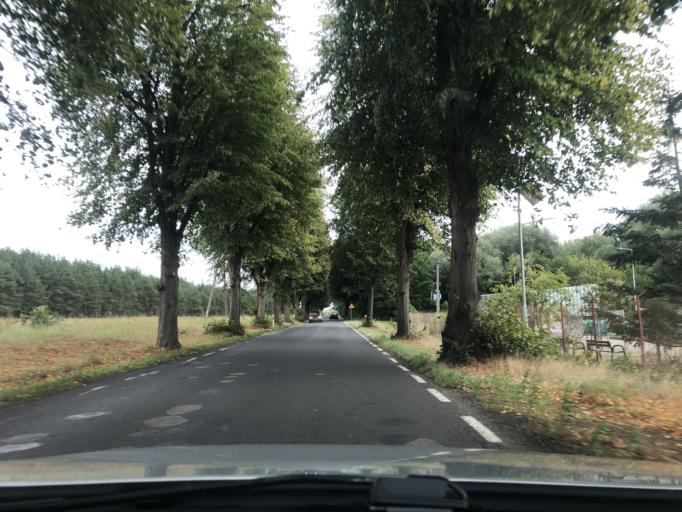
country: PL
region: Greater Poland Voivodeship
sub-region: Powiat czarnkowsko-trzcianecki
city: Wielen
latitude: 52.9041
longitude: 16.1575
